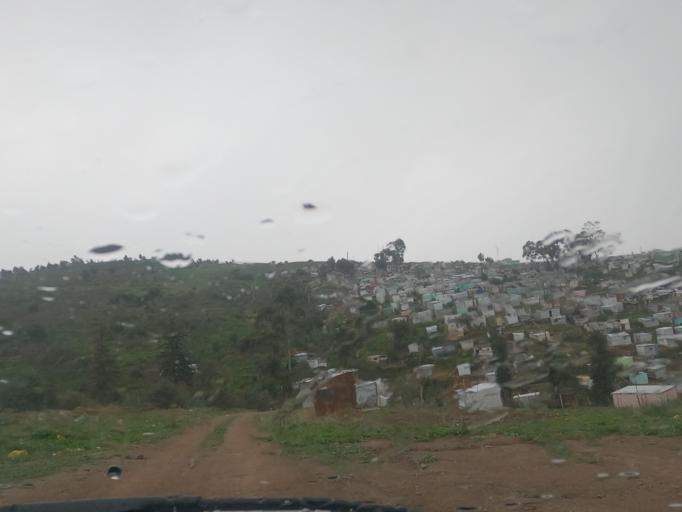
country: ZA
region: Western Cape
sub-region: Cape Winelands District Municipality
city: Stellenbosch
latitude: -33.9263
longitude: 18.8442
